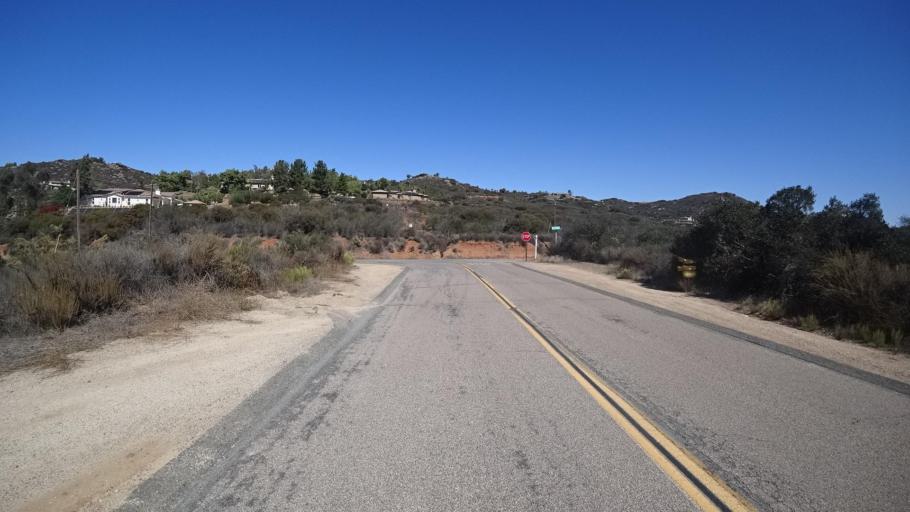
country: US
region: California
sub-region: San Diego County
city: Alpine
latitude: 32.8019
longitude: -116.7706
